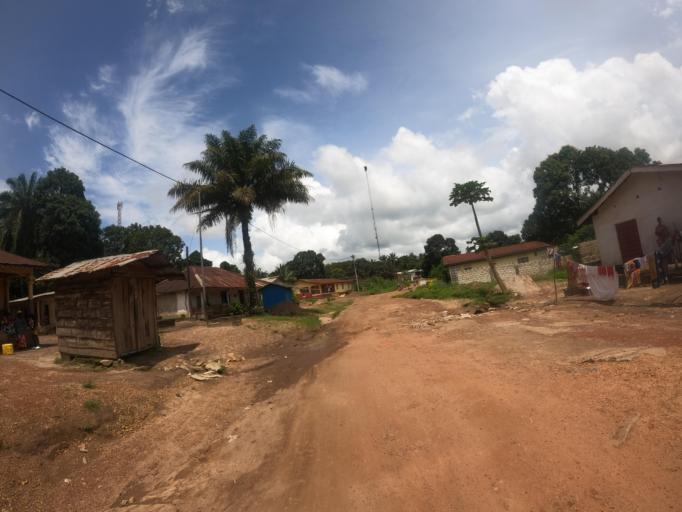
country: SL
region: Northern Province
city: Makeni
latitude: 8.8941
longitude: -12.0562
